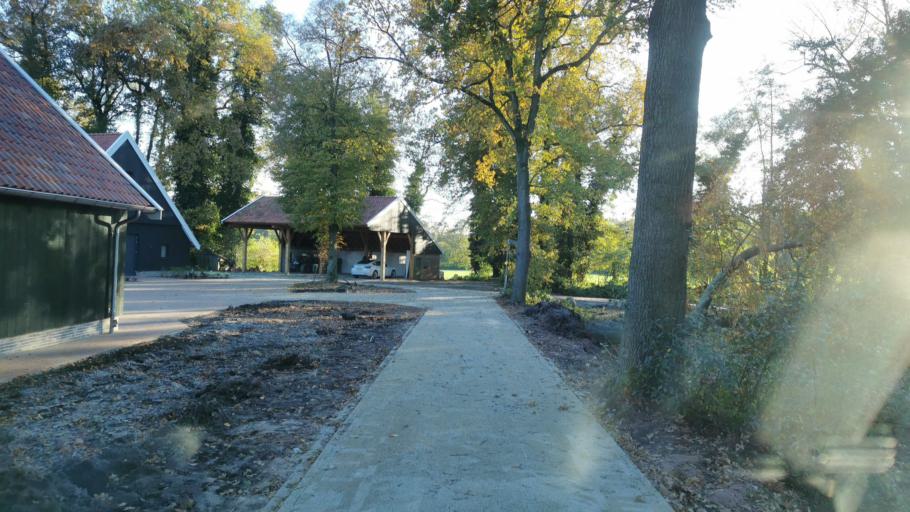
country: NL
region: Overijssel
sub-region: Gemeente Oldenzaal
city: Oldenzaal
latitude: 52.3154
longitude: 6.9808
